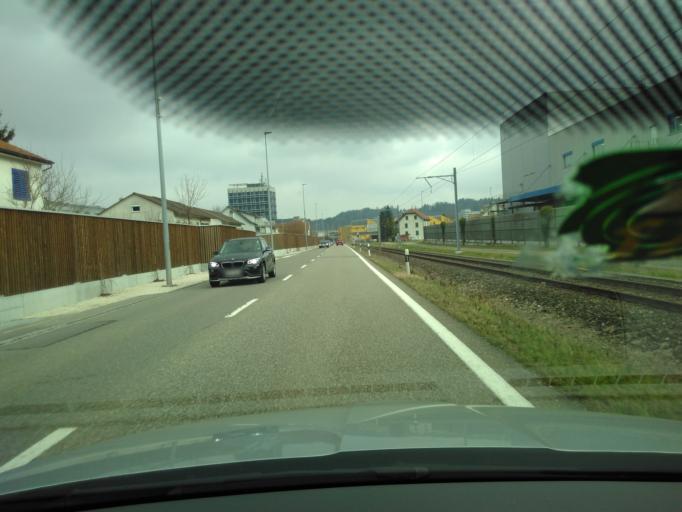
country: CH
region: Aargau
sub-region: Bezirk Aarau
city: Suhr
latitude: 47.3675
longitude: 8.0760
